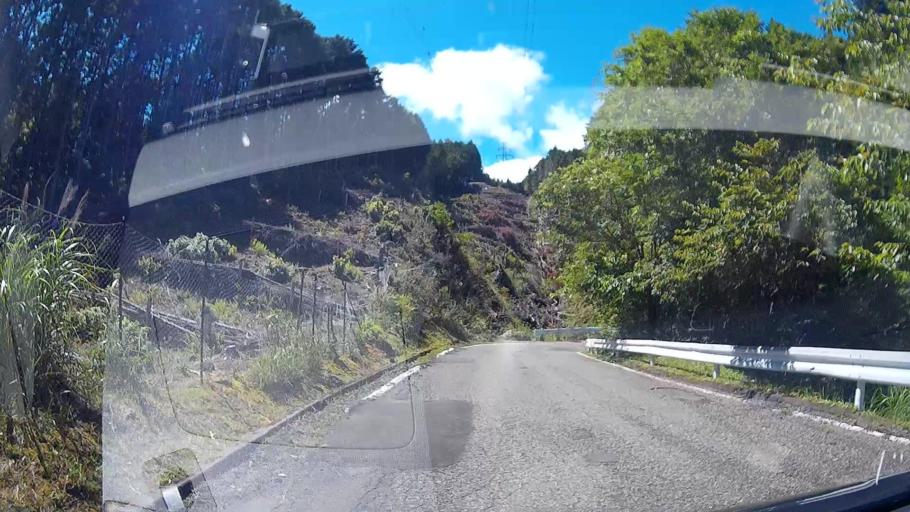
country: JP
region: Shizuoka
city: Shizuoka-shi
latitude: 35.1966
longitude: 138.2599
